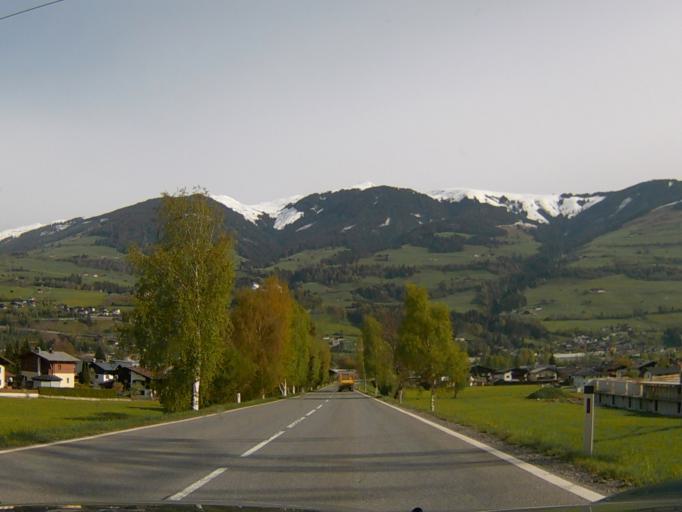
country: AT
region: Salzburg
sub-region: Politischer Bezirk Zell am See
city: Mittersill
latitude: 47.2712
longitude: 12.4873
